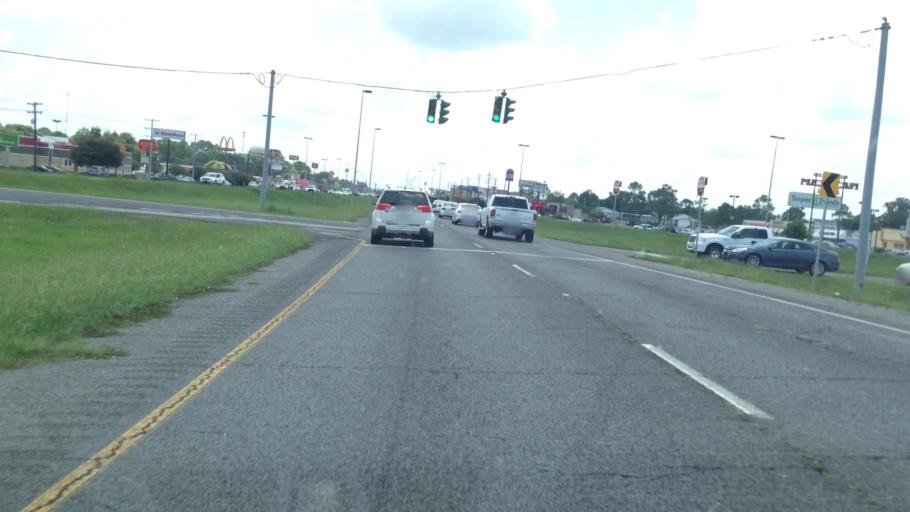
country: US
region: Louisiana
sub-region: Rapides Parish
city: Alexandria
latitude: 31.2992
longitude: -92.4801
